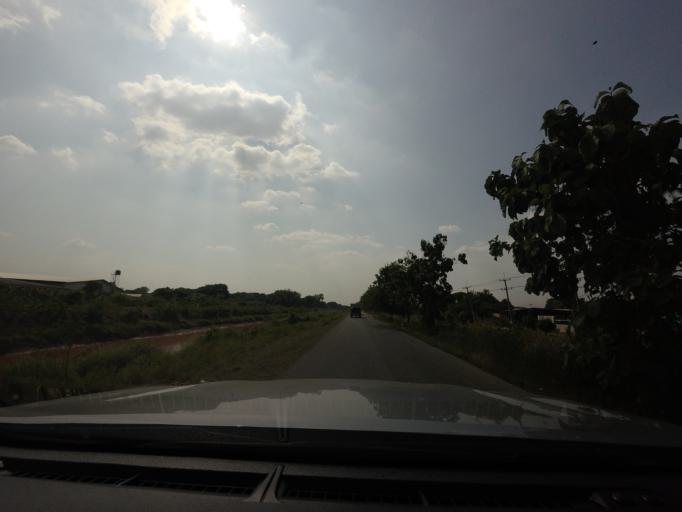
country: TH
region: Phitsanulok
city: Phitsanulok
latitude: 16.8097
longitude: 100.2218
